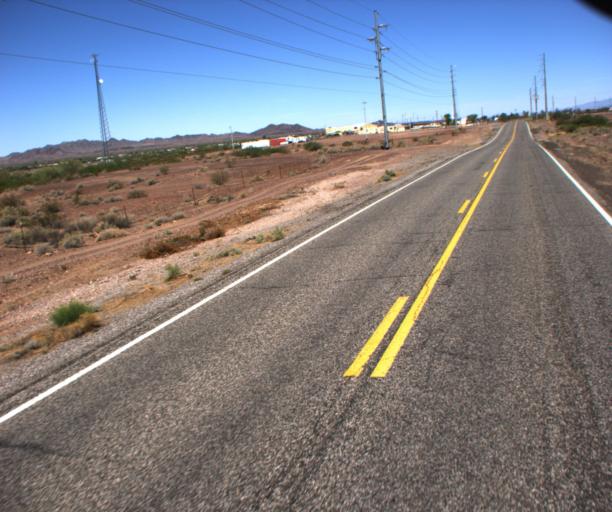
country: US
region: Arizona
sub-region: La Paz County
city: Quartzsite
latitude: 33.9103
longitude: -113.9867
